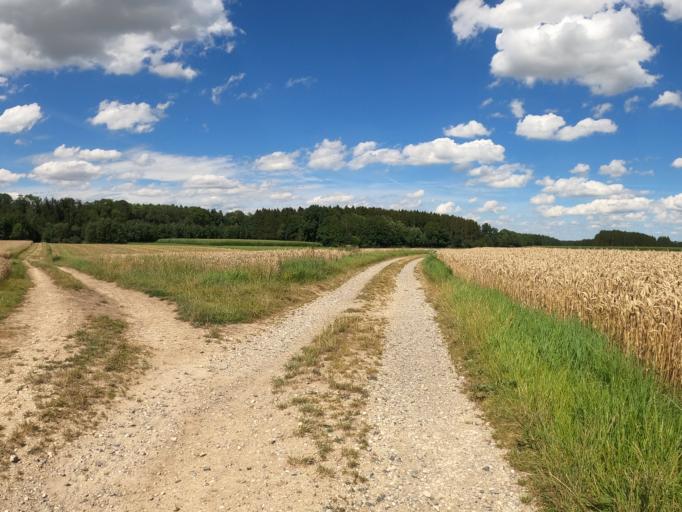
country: DE
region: Bavaria
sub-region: Swabia
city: Leipheim
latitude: 48.4058
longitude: 10.2127
